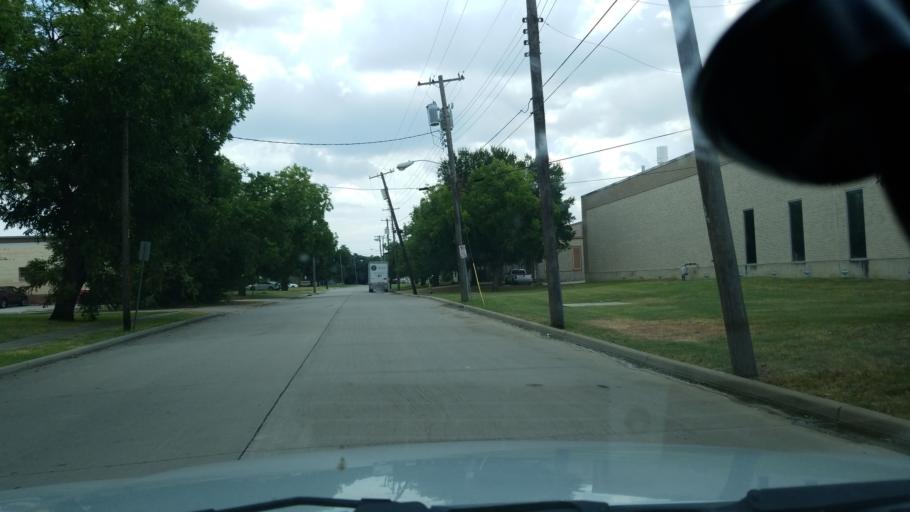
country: US
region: Texas
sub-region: Dallas County
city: Irving
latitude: 32.8361
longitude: -96.8818
